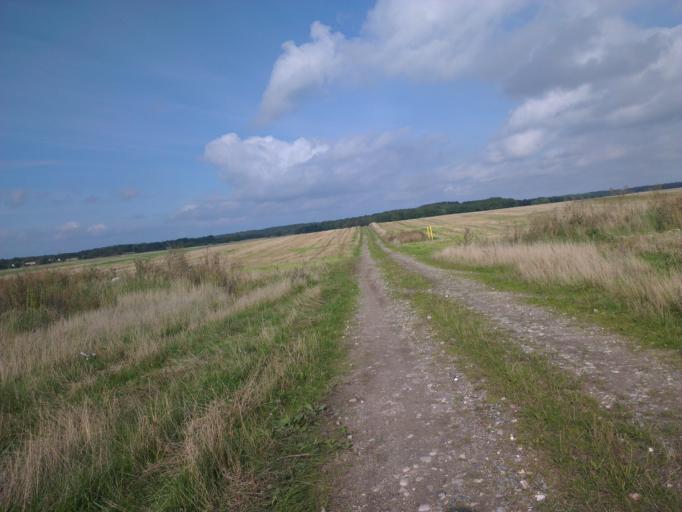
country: DK
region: Capital Region
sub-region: Frederikssund Kommune
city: Jaegerspris
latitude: 55.8785
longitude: 11.9623
